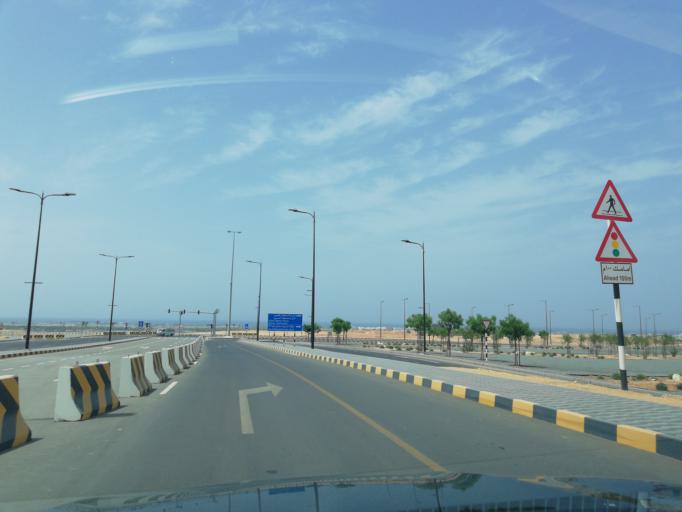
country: OM
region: Muhafazat Masqat
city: Bawshar
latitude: 23.5671
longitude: 58.3214
